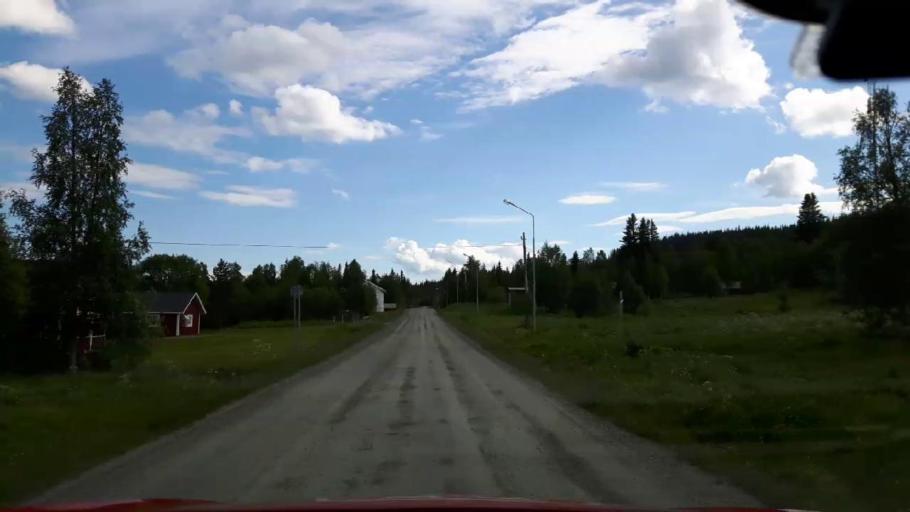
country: SE
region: Jaemtland
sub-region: Krokoms Kommun
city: Valla
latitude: 63.8263
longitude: 14.0407
